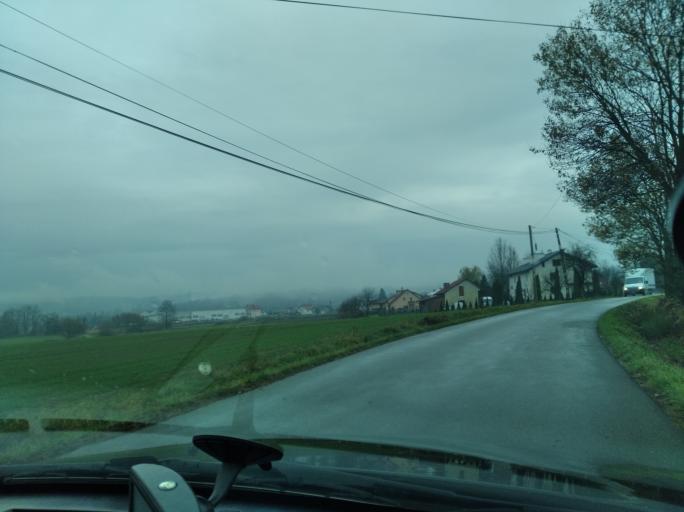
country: PL
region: Subcarpathian Voivodeship
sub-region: Powiat strzyzowski
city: Babica
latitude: 49.9275
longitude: 21.8559
